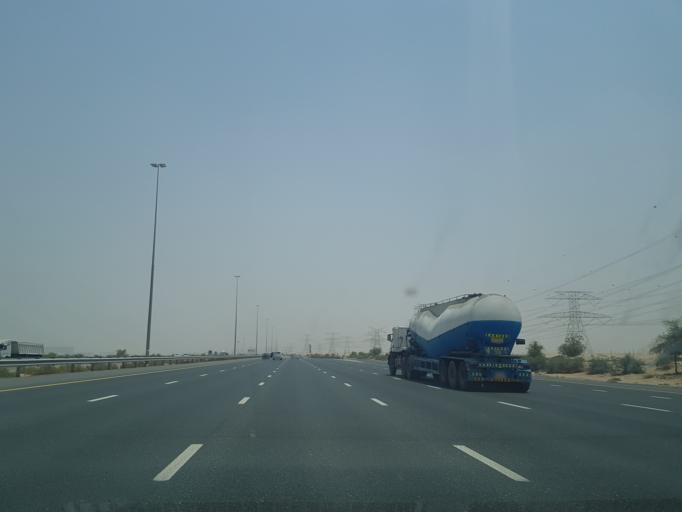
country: AE
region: Dubai
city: Dubai
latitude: 25.0656
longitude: 55.3425
